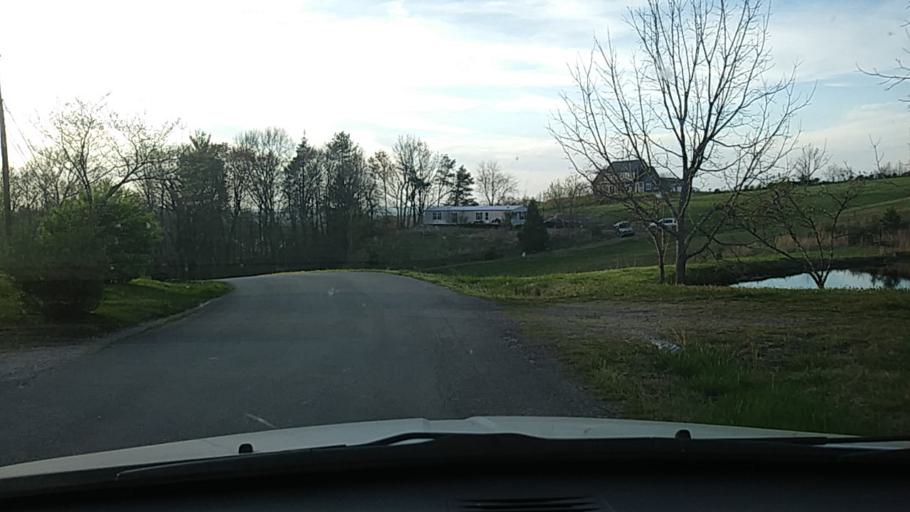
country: US
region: Tennessee
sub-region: Greene County
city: Tusculum
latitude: 36.0943
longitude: -82.7040
